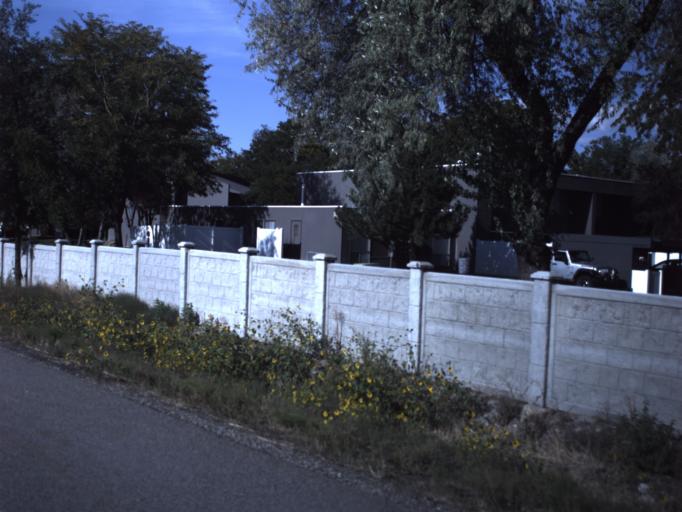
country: US
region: Utah
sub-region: Salt Lake County
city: Holladay
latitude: 40.6566
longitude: -111.8521
